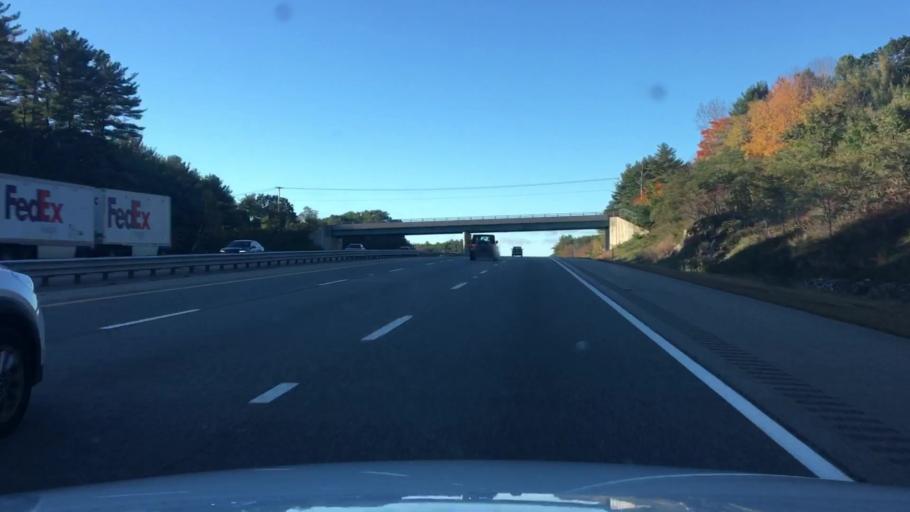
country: US
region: Maine
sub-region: York County
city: West Kennebunk
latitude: 43.3980
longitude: -70.5667
